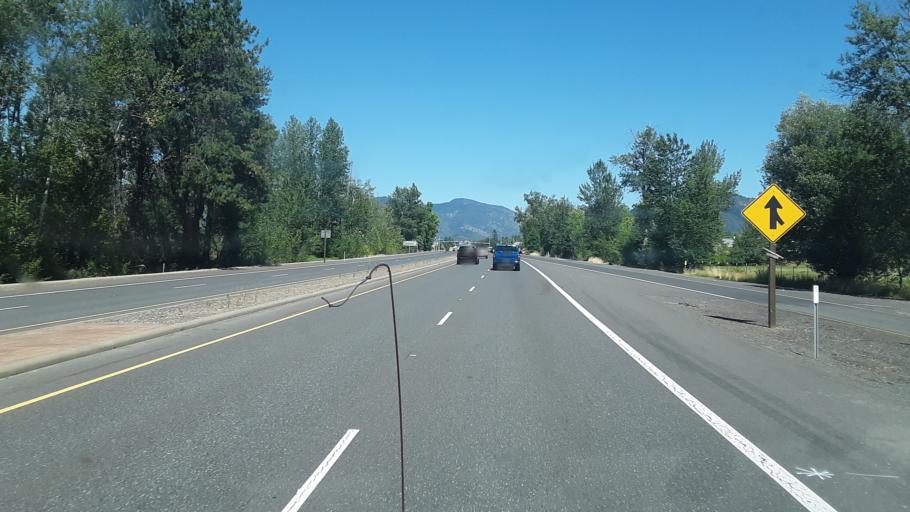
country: US
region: Oregon
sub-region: Josephine County
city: Redwood
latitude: 42.4174
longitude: -123.3736
